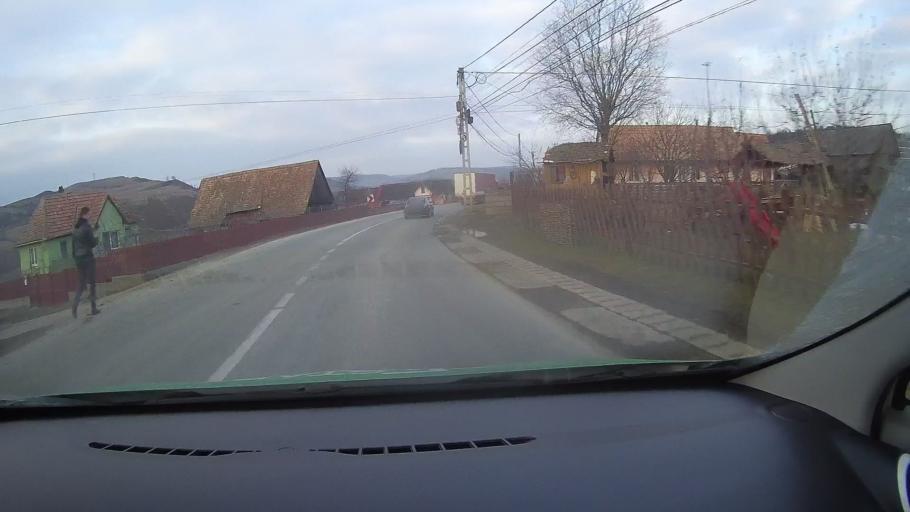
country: RO
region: Harghita
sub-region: Comuna Simonesti
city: Simonesti
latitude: 46.3432
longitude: 25.1156
